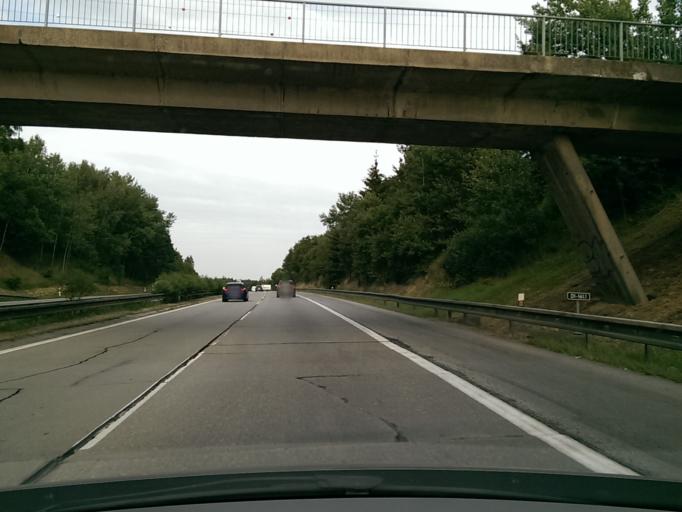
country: CZ
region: Vysocina
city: Kamenice
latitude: 49.4073
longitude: 15.7810
